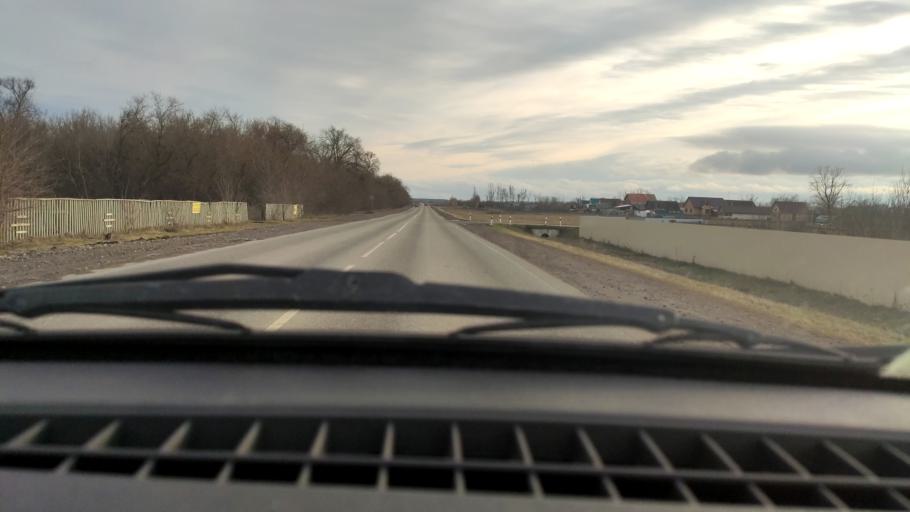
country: RU
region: Bashkortostan
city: Davlekanovo
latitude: 54.2933
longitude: 55.1236
